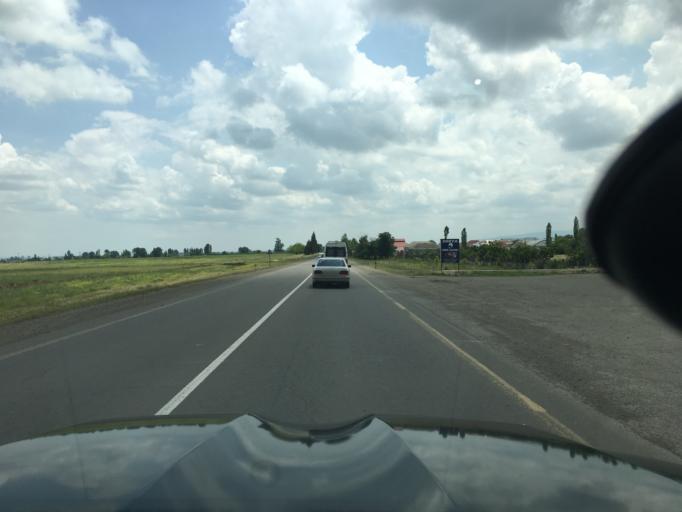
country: AZ
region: Tovuz
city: Tovuz
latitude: 40.9560
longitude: 45.7351
